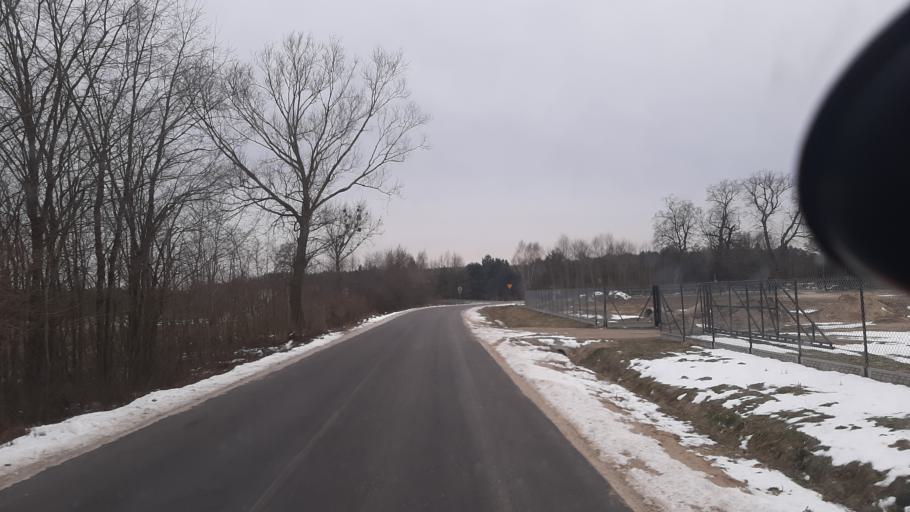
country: PL
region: Lublin Voivodeship
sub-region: Powiat lubartowski
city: Kamionka
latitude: 51.4867
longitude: 22.4483
